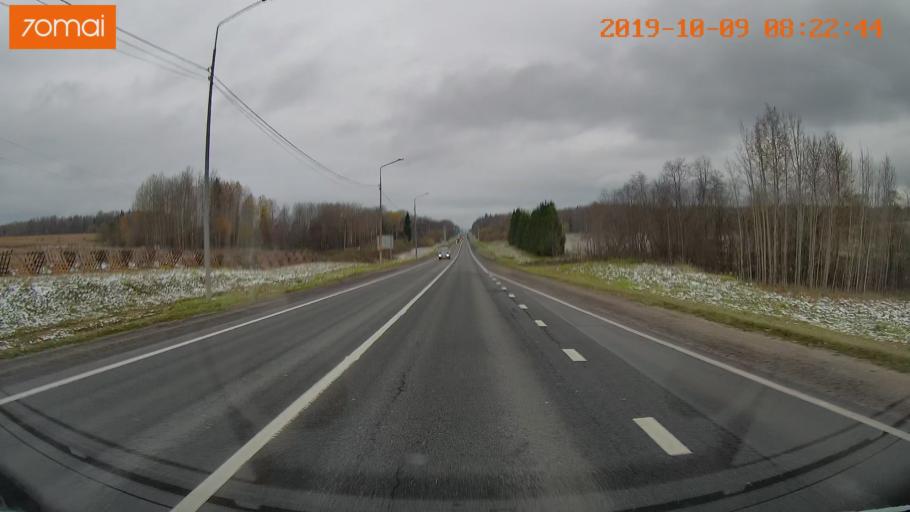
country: RU
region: Vologda
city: Gryazovets
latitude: 58.7456
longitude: 40.2871
